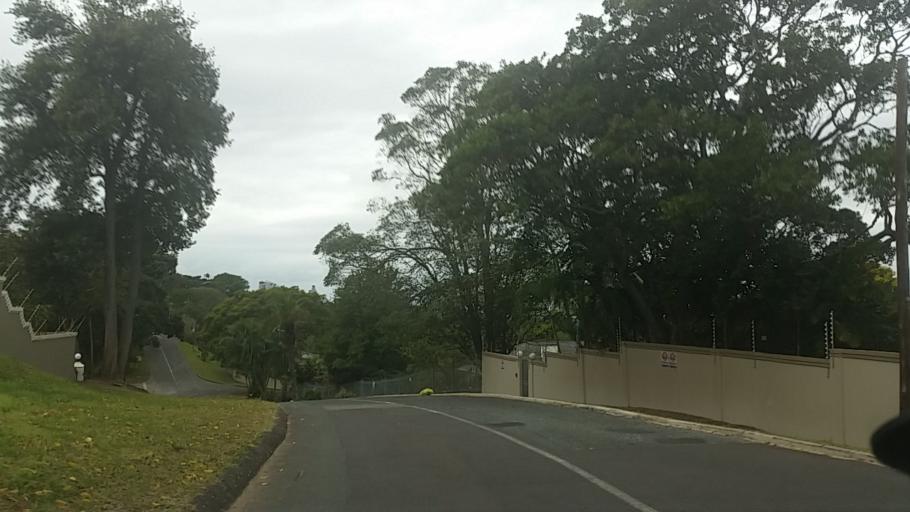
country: ZA
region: KwaZulu-Natal
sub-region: eThekwini Metropolitan Municipality
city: Berea
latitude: -29.8389
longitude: 30.9304
